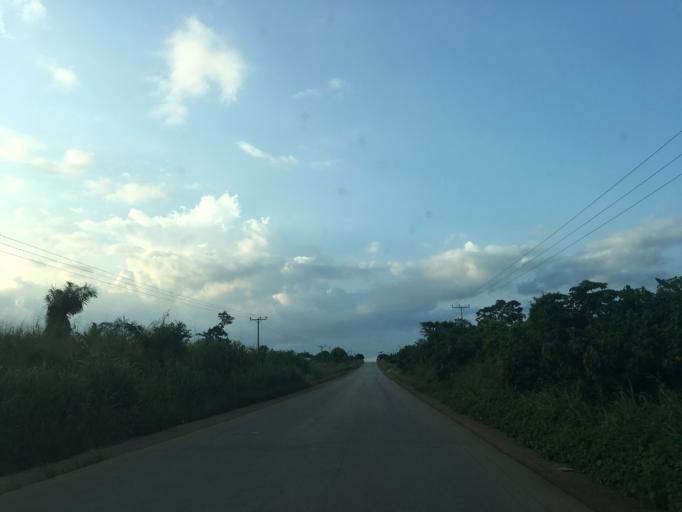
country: GH
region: Western
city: Bibiani
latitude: 6.6390
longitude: -2.4252
